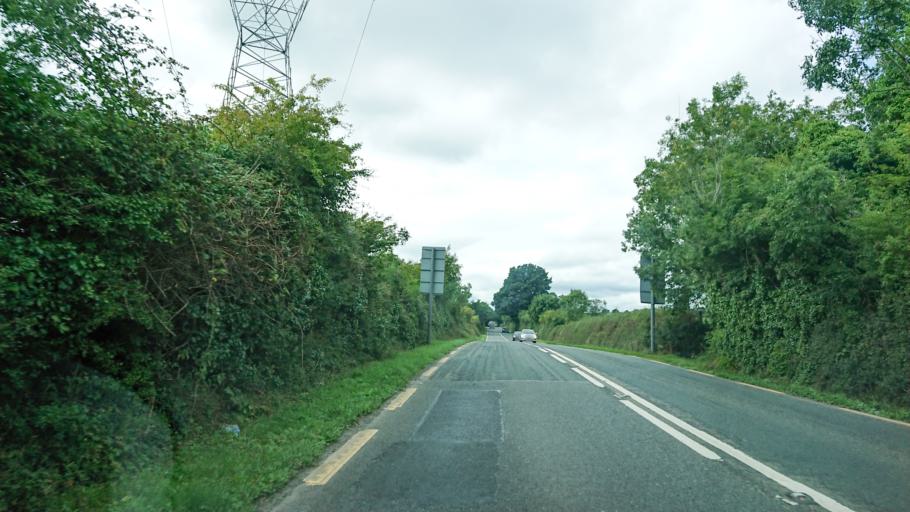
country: IE
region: Munster
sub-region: Waterford
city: Dungarvan
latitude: 52.1098
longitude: -7.6795
